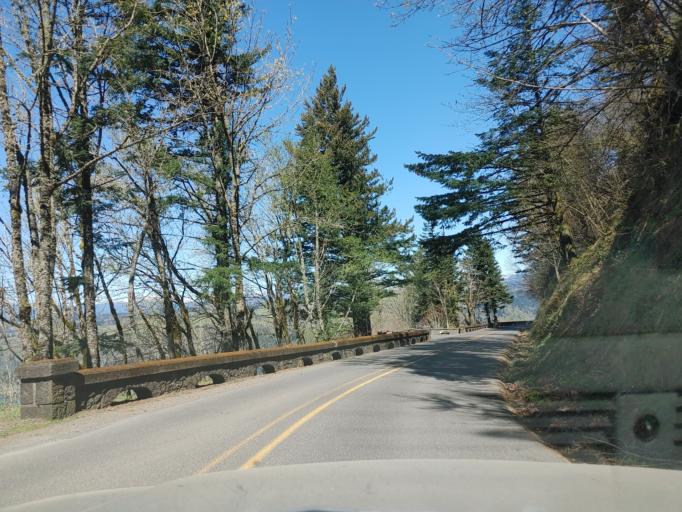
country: US
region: Washington
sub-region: Clark County
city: Washougal
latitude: 45.5375
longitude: -122.2475
